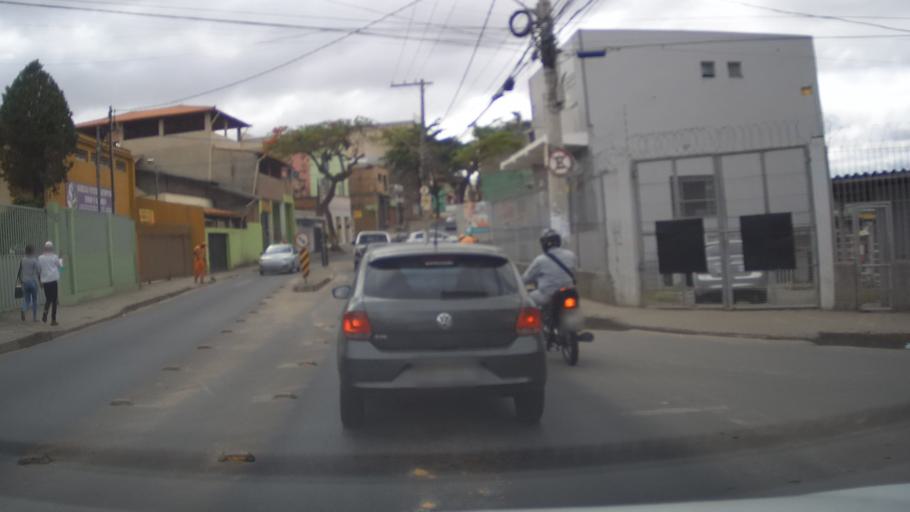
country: BR
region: Minas Gerais
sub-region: Belo Horizonte
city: Belo Horizonte
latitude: -19.8441
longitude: -43.9461
